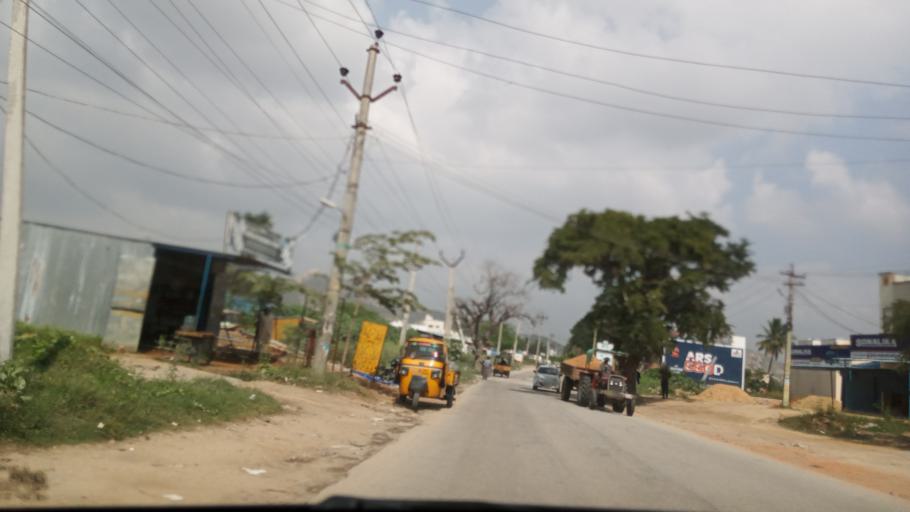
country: IN
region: Andhra Pradesh
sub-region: Chittoor
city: Madanapalle
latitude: 13.5686
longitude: 78.5147
